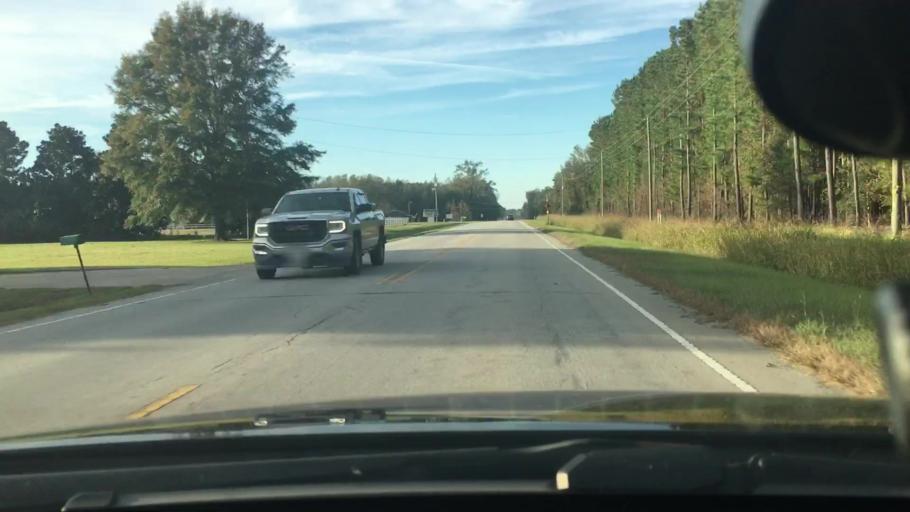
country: US
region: North Carolina
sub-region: Pitt County
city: Windsor
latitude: 35.4843
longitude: -77.3020
